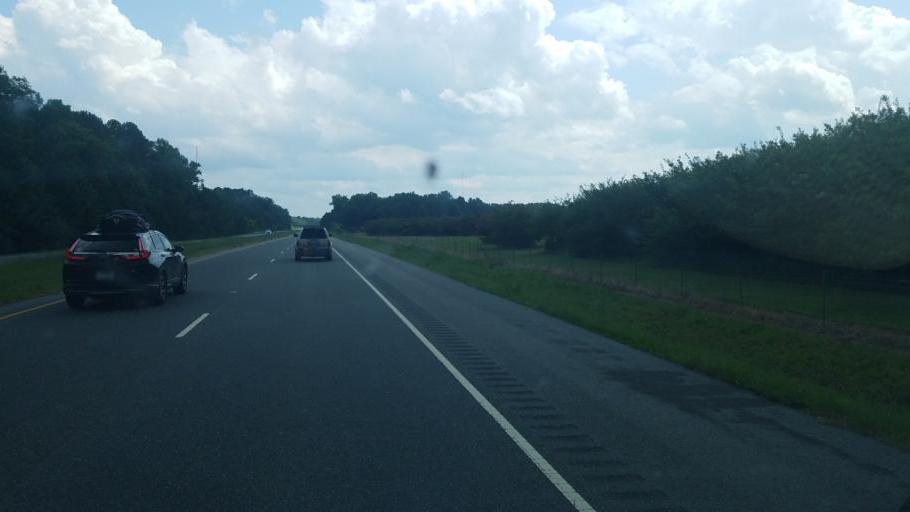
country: US
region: North Carolina
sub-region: Currituck County
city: Moyock
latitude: 36.6425
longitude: -76.2197
